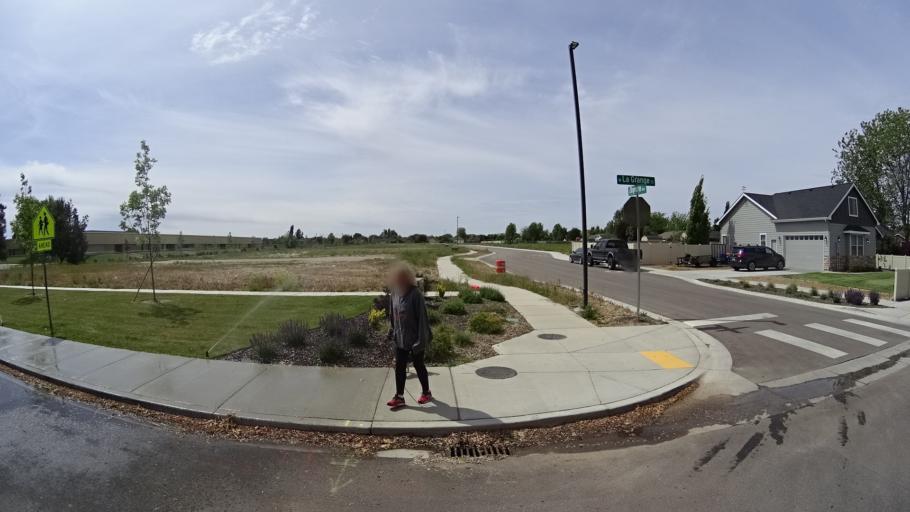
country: US
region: Idaho
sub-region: Ada County
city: Meridian
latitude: 43.5539
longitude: -116.3286
